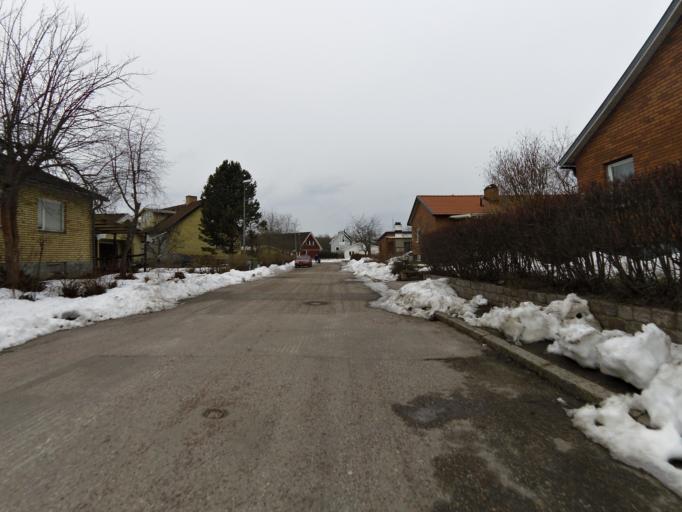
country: SE
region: Gaevleborg
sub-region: Gavle Kommun
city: Gavle
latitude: 60.6602
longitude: 17.1235
